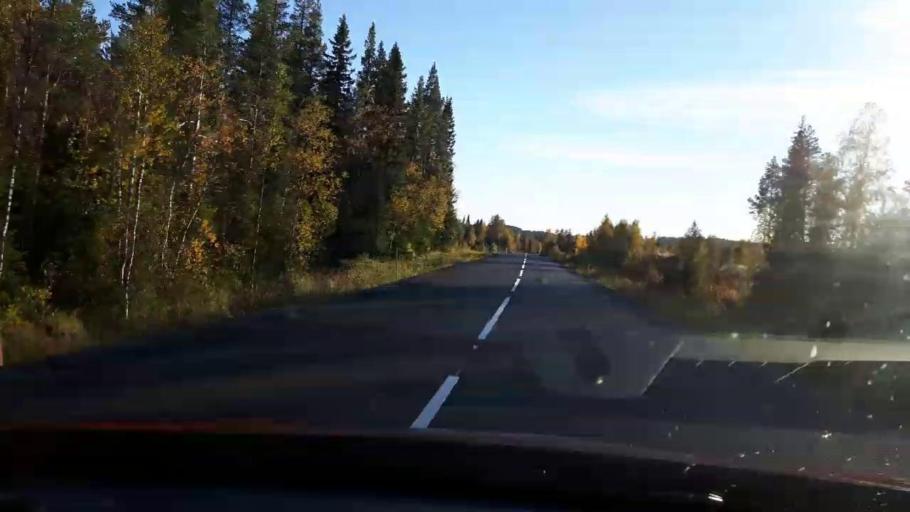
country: SE
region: Jaemtland
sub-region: OEstersunds Kommun
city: Lit
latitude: 63.5517
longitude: 14.8843
